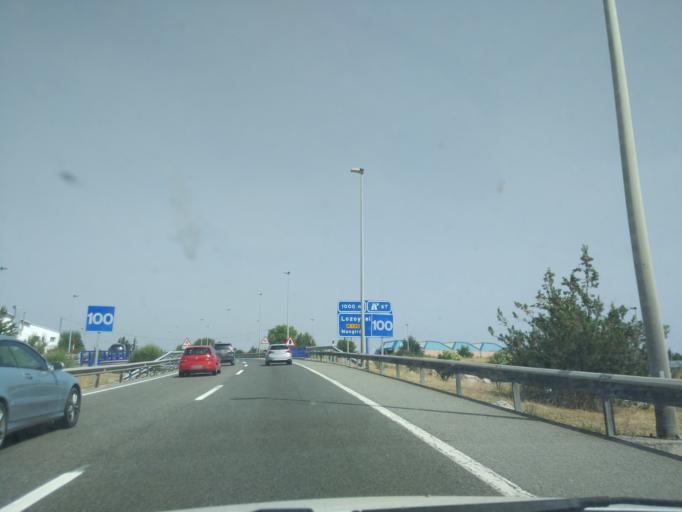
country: ES
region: Madrid
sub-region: Provincia de Madrid
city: La Cabrera
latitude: 40.9203
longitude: -3.6119
